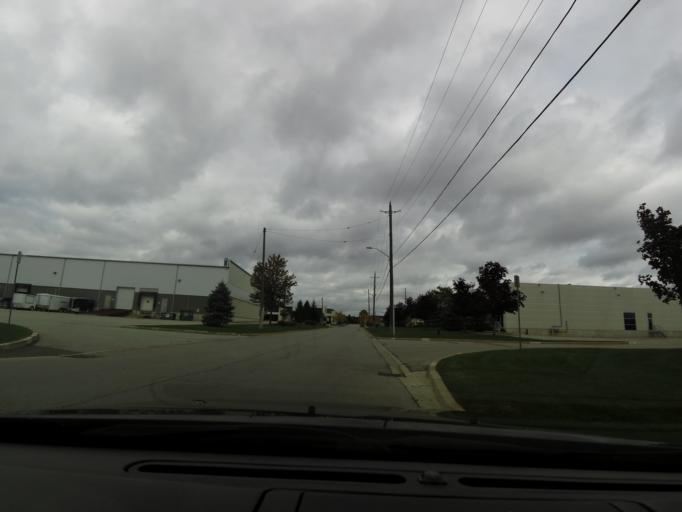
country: CA
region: Ontario
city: Burlington
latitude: 43.3893
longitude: -79.7766
